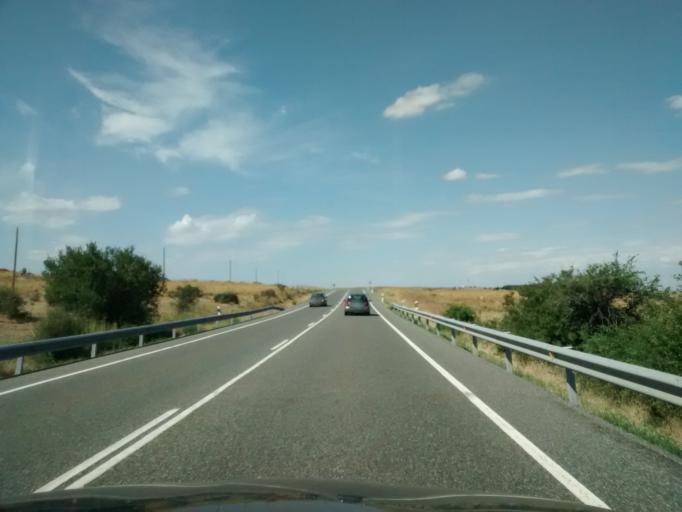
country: ES
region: Castille and Leon
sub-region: Provincia de Segovia
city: Santo Domingo de Piron
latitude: 41.0187
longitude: -3.9676
